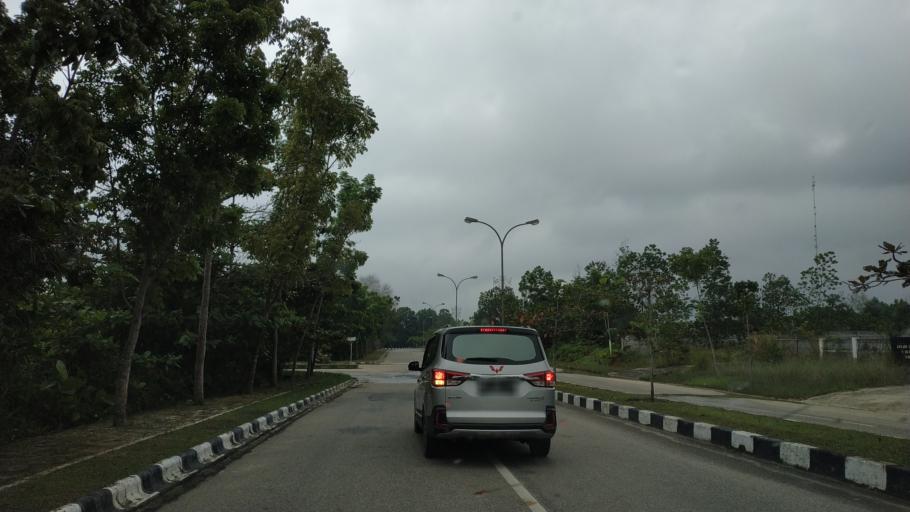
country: ID
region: Riau
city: Pangkalanbunut
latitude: 0.3828
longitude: 101.8240
